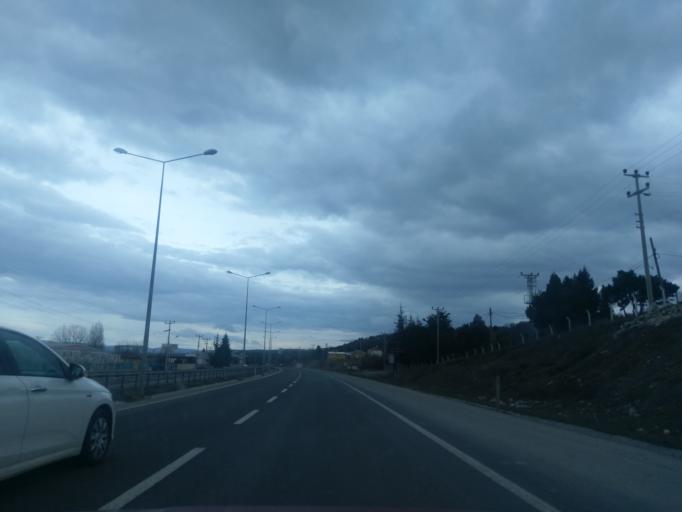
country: TR
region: Kuetahya
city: Kutahya
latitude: 39.3783
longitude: 30.0506
